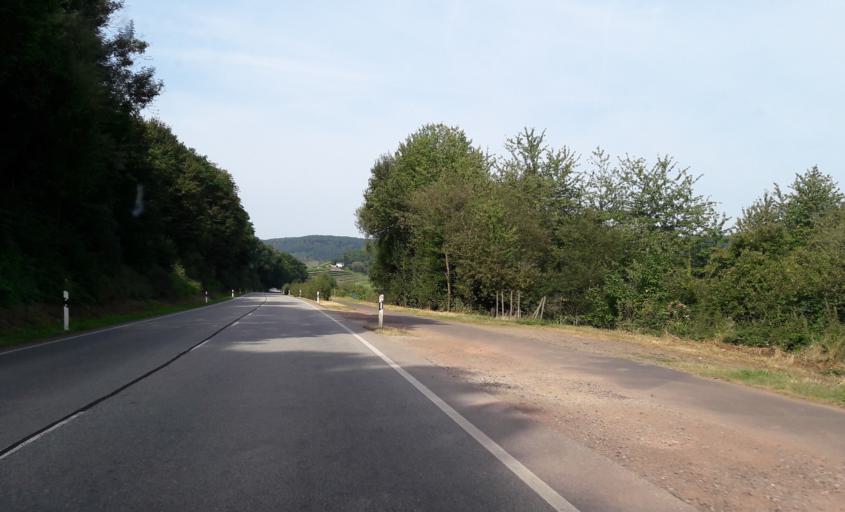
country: DE
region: Rheinland-Pfalz
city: Zell
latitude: 50.0388
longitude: 7.1604
